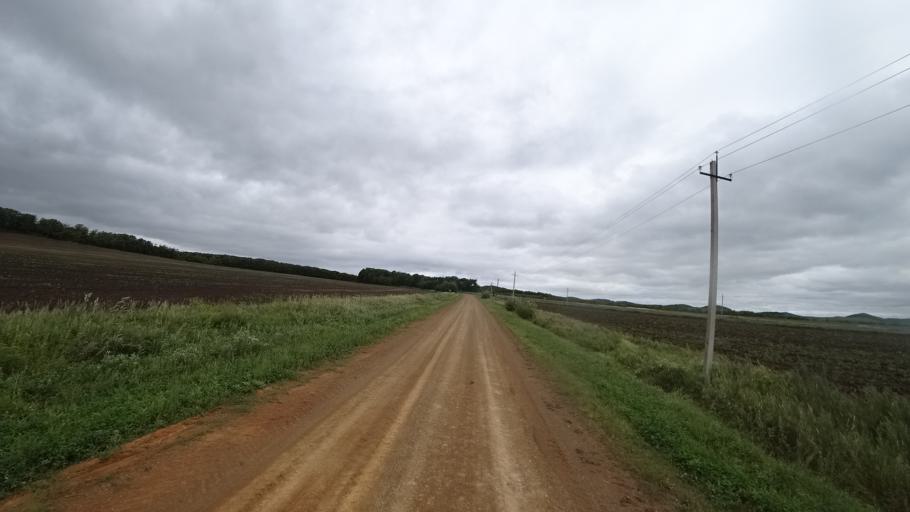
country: RU
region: Primorskiy
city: Chernigovka
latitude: 44.4477
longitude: 132.5969
